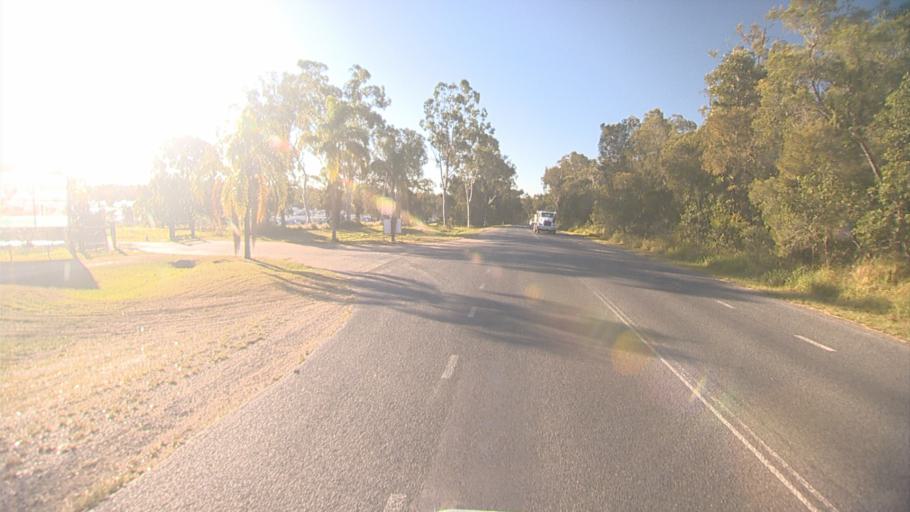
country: AU
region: Queensland
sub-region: Logan
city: Logan Reserve
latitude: -27.7257
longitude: 153.0900
